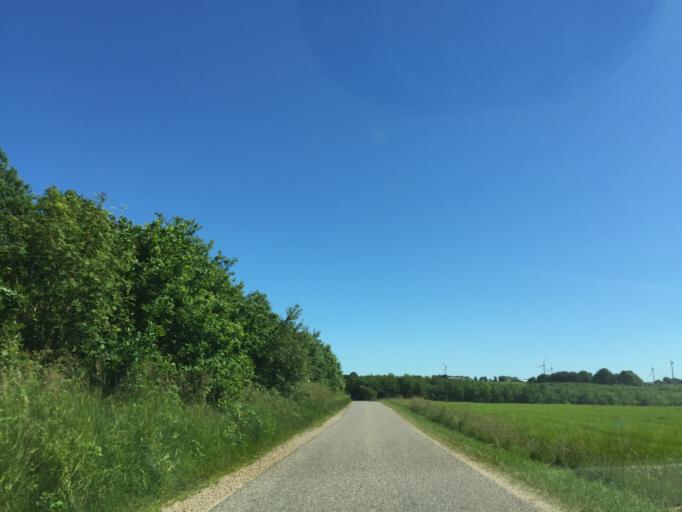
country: DK
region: Central Jutland
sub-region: Viborg Kommune
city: Bjerringbro
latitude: 56.2708
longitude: 9.6905
